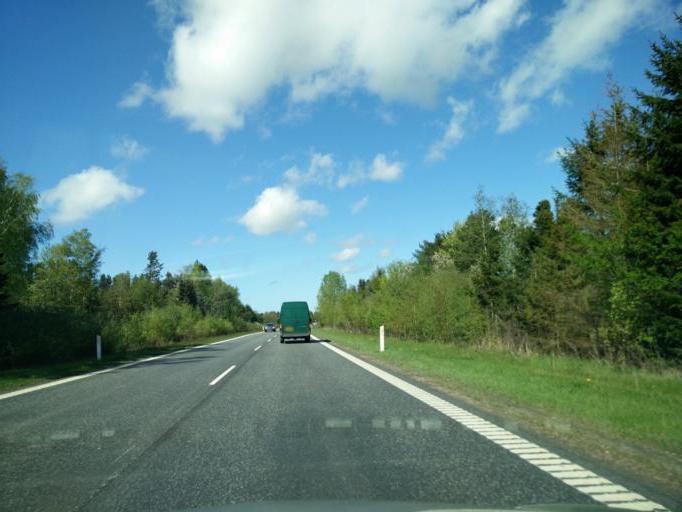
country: DK
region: Capital Region
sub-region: Hillerod Kommune
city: Hillerod
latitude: 55.9429
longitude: 12.2447
